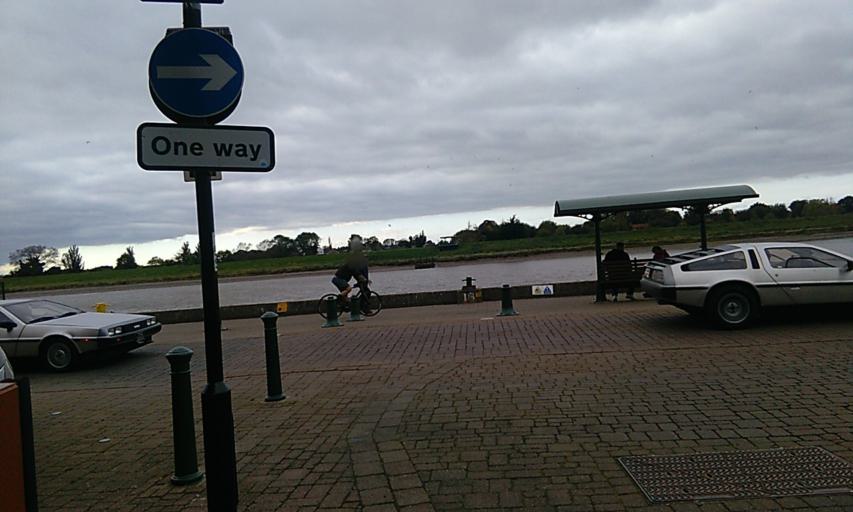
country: GB
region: England
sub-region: Norfolk
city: King's Lynn
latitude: 52.7518
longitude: 0.3936
